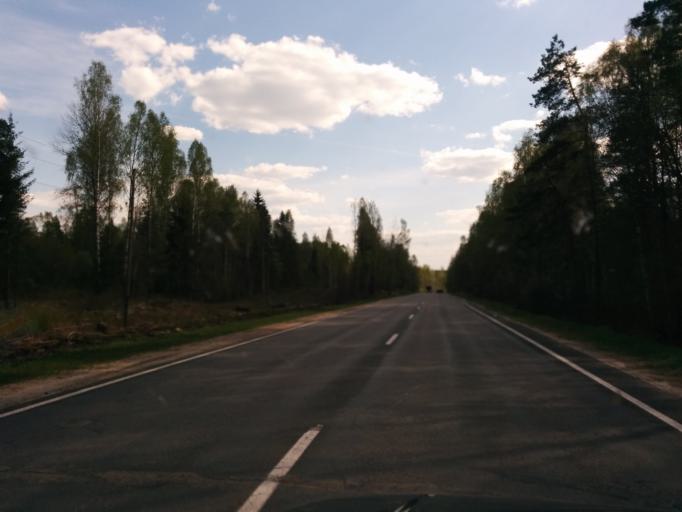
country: LV
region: Pargaujas
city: Stalbe
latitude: 57.3052
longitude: 24.9251
